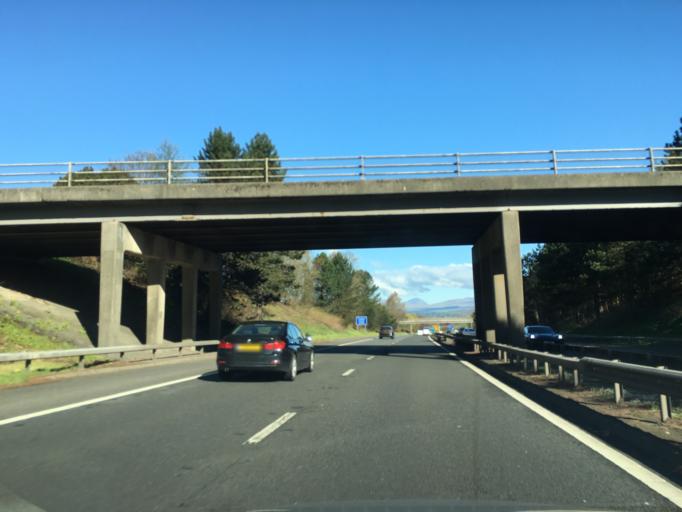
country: GB
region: Scotland
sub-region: Stirling
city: Stirling
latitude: 56.1099
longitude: -3.9620
